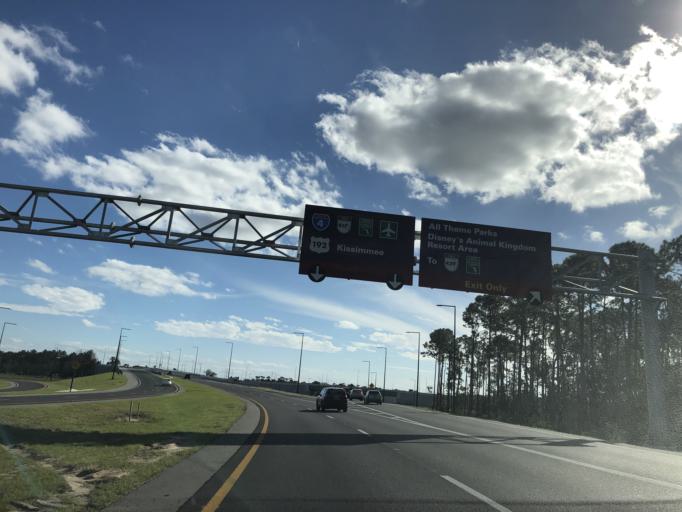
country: US
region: Florida
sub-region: Osceola County
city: Celebration
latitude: 28.3520
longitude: -81.5532
